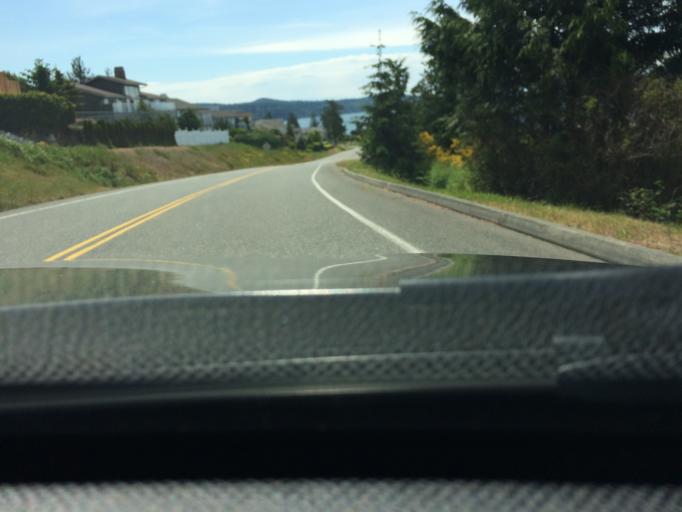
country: US
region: Washington
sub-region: Skagit County
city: Anacortes
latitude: 48.4926
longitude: -122.6703
